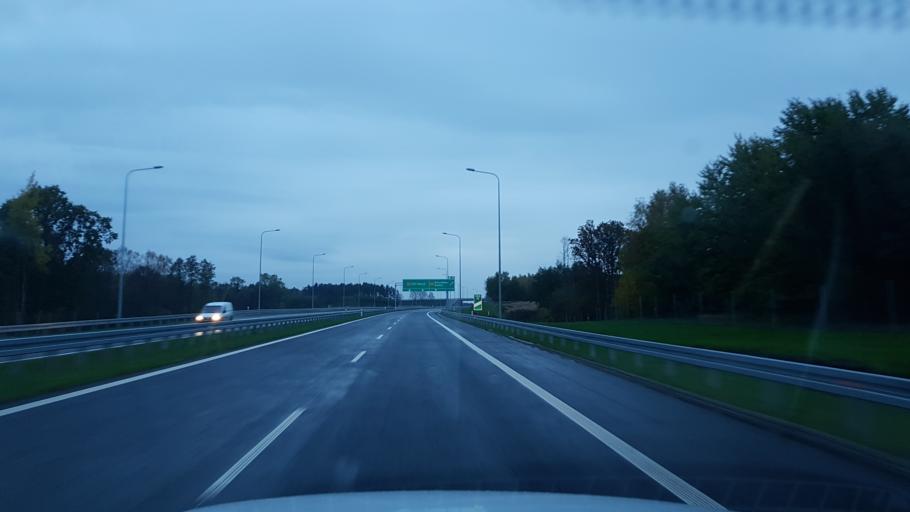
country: PL
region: West Pomeranian Voivodeship
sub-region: Powiat gryficki
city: Brojce
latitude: 53.9377
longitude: 15.3945
